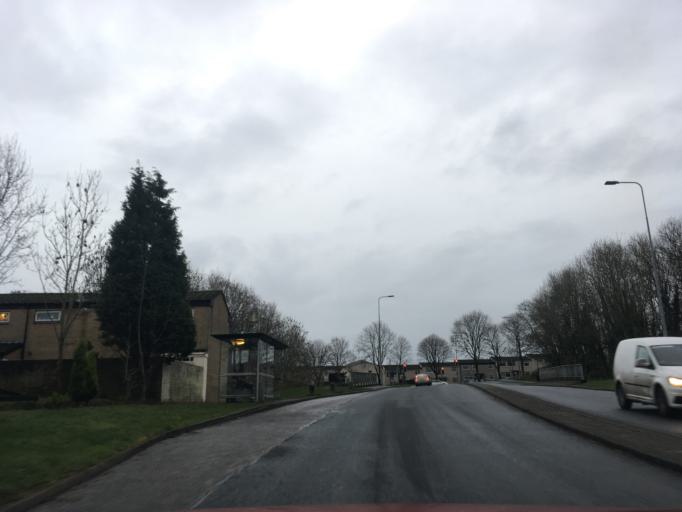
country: GB
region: Wales
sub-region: Cardiff
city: Cardiff
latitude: 51.5199
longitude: -3.1535
